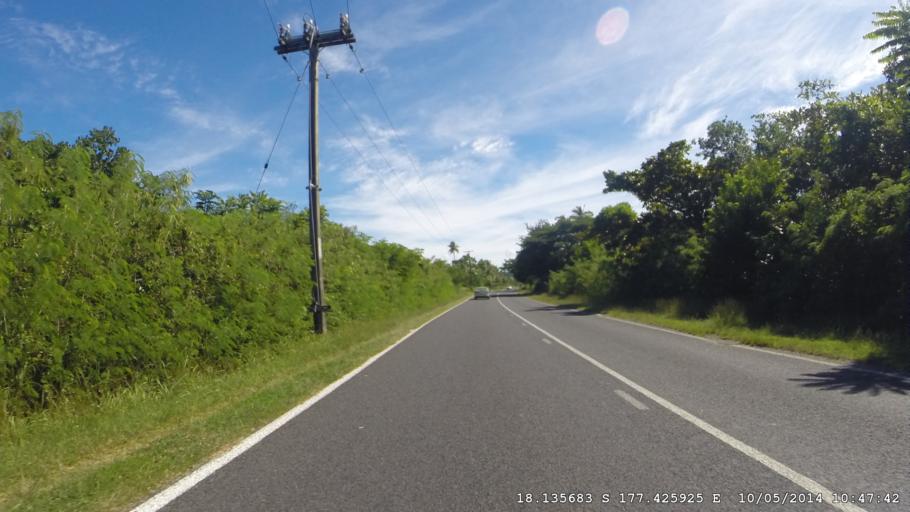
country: FJ
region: Western
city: Nadi
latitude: -18.1357
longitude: 177.4259
